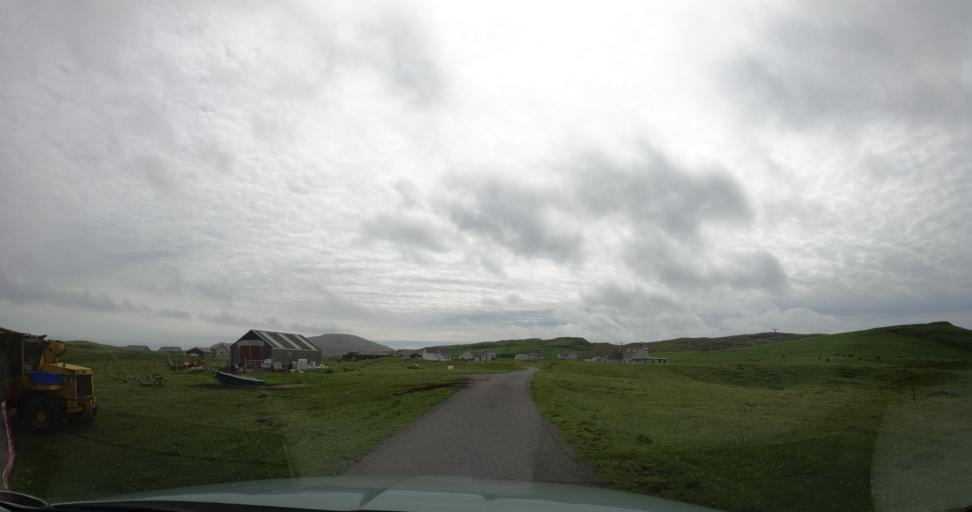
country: GB
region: Scotland
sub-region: Eilean Siar
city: Barra
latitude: 56.9213
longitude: -7.5376
